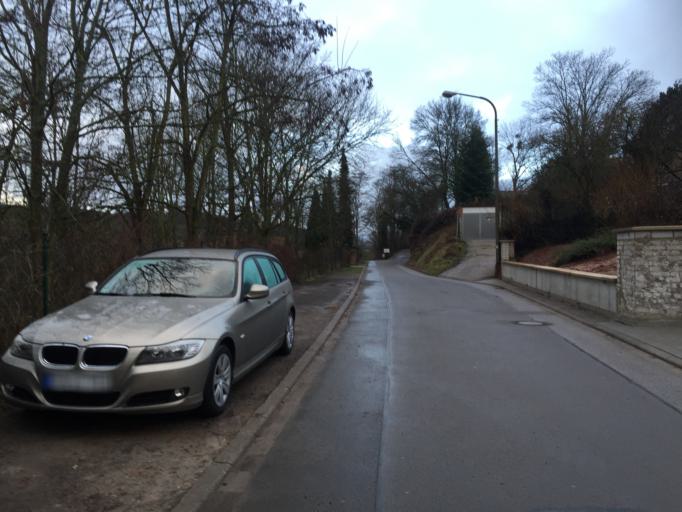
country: DE
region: Rheinland-Pfalz
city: Neuleiningen
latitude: 49.5420
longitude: 8.1332
